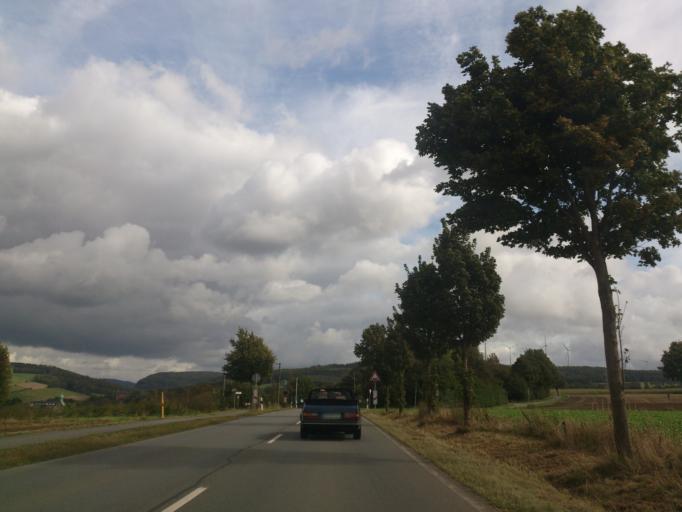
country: DE
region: North Rhine-Westphalia
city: Bad Lippspringe
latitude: 51.7422
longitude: 8.8395
